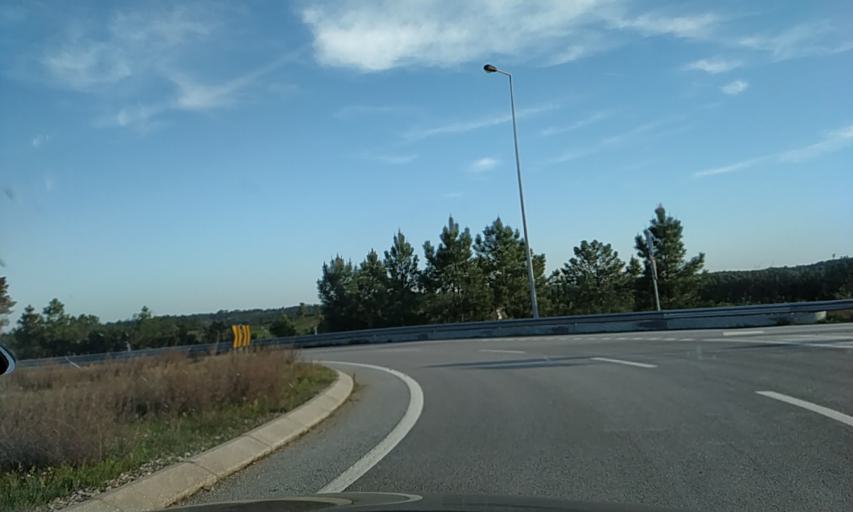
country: PT
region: Castelo Branco
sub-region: Castelo Branco
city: Castelo Branco
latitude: 39.7583
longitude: -7.6054
